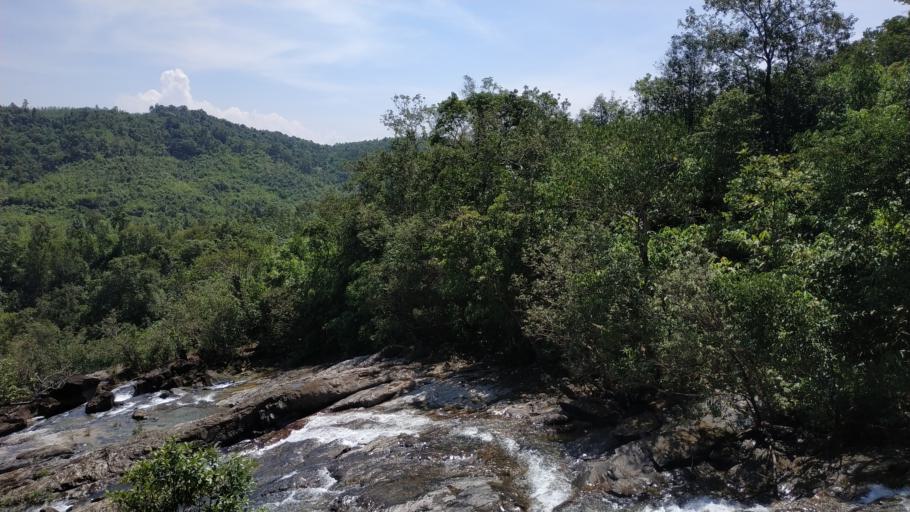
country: MM
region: Tanintharyi
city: Dawei
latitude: 14.5838
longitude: 98.0488
